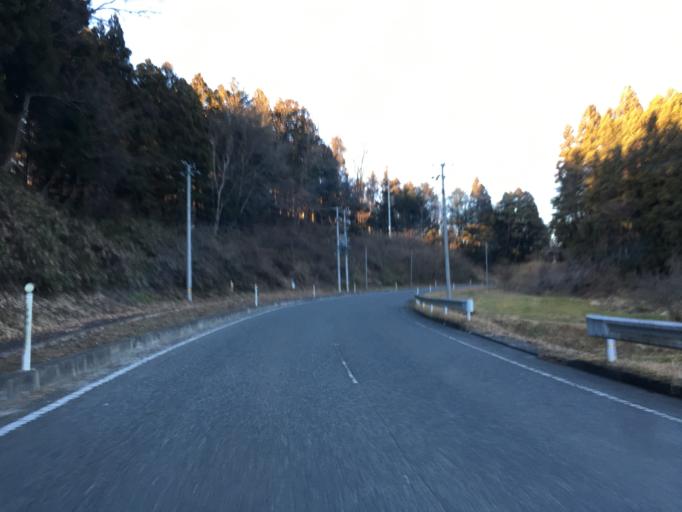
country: JP
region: Fukushima
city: Ishikawa
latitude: 37.2010
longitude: 140.5579
